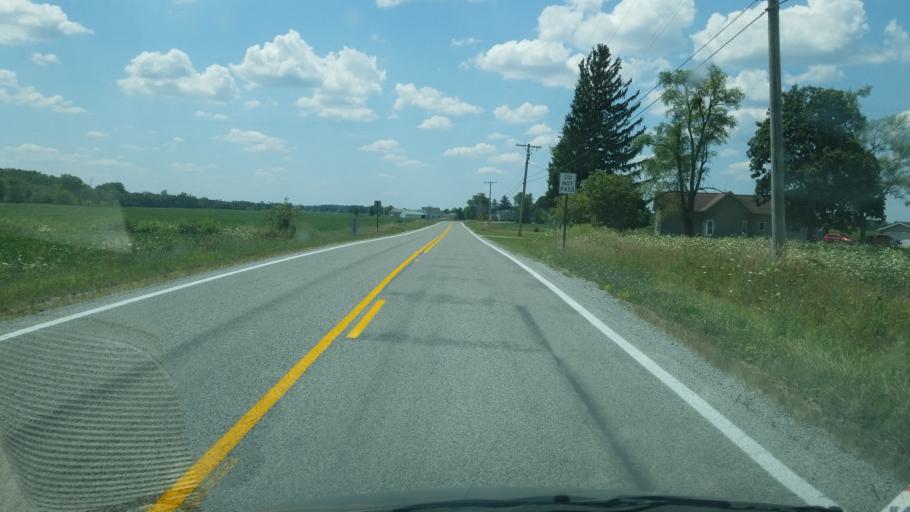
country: US
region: Ohio
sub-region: Champaign County
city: Mechanicsburg
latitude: 40.1180
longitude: -83.4722
